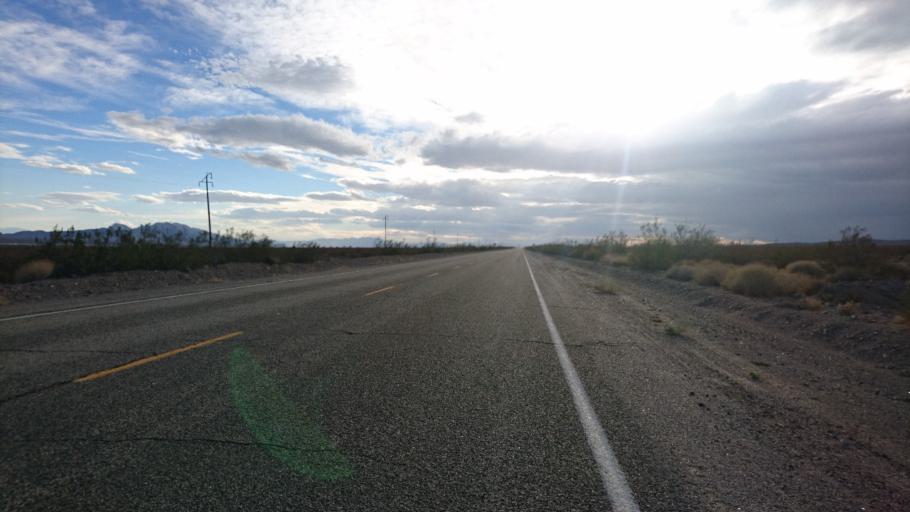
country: US
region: California
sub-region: San Bernardino County
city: Needles
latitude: 34.6728
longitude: -115.3368
